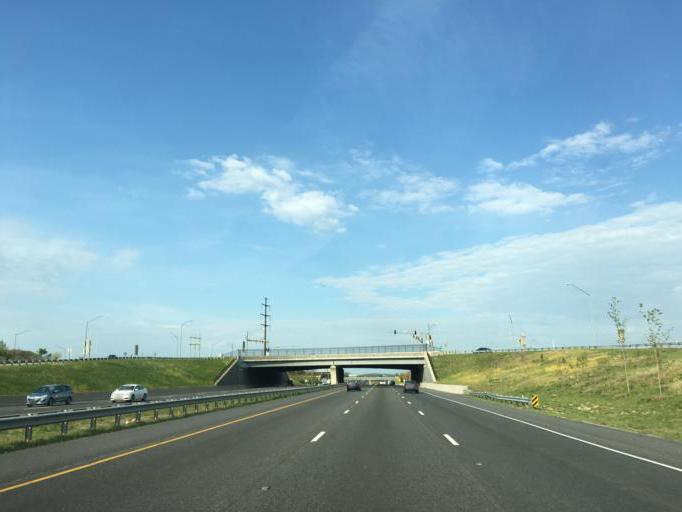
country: US
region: Maryland
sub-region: Frederick County
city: Frederick
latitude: 39.4020
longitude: -77.4017
